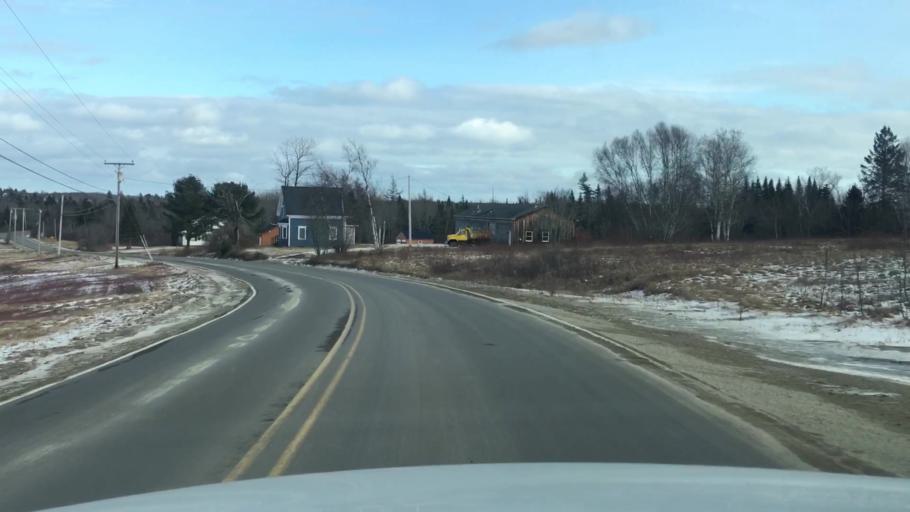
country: US
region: Maine
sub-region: Washington County
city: Jonesport
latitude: 44.6082
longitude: -67.5972
